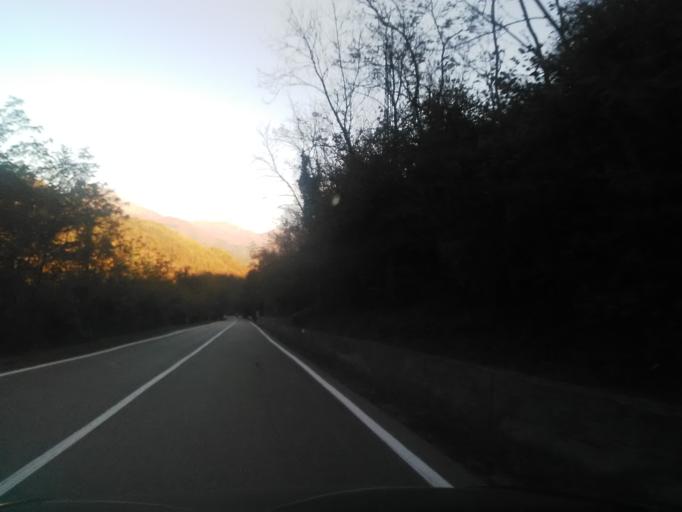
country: IT
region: Piedmont
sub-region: Provincia di Biella
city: Crevacuore
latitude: 45.6705
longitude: 8.2576
